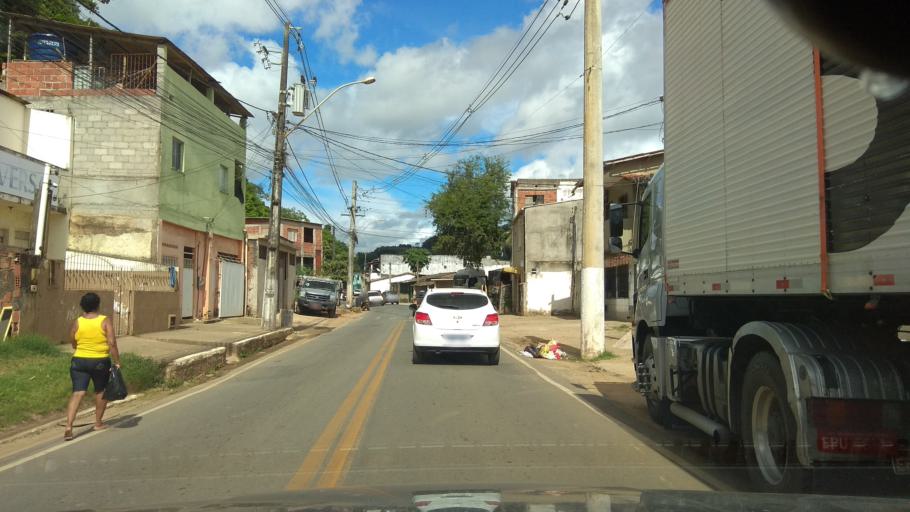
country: BR
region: Bahia
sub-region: Ilheus
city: Ilheus
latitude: -14.7907
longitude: -39.0617
